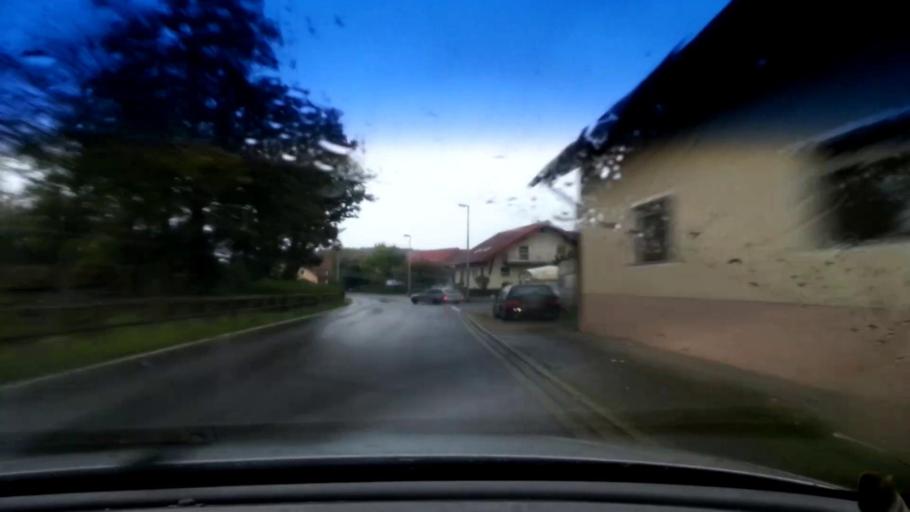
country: DE
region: Bavaria
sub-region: Upper Franconia
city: Walsdorf
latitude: 49.8700
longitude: 10.7796
